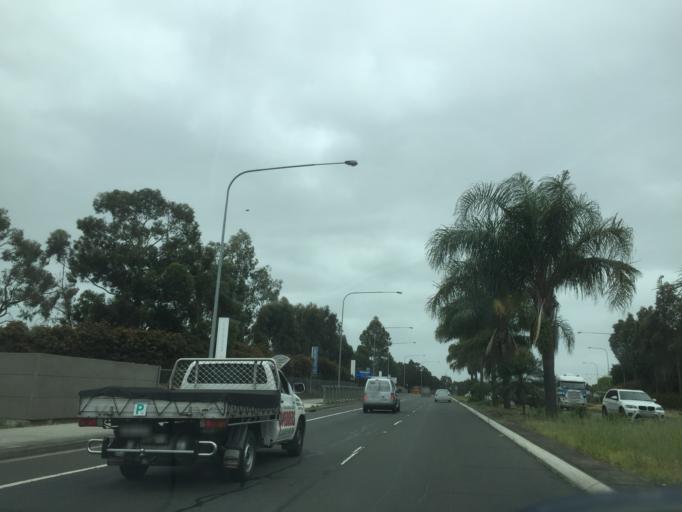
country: AU
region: New South Wales
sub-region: Blacktown
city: Stanhope Gardens
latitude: -33.7231
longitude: 150.9301
